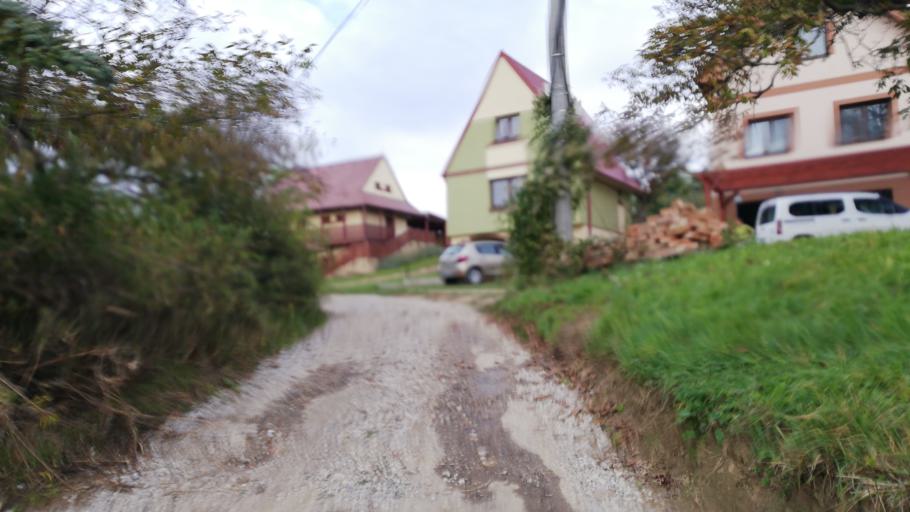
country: SK
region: Trnavsky
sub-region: Okres Skalica
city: Skalica
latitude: 48.8203
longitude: 17.2374
